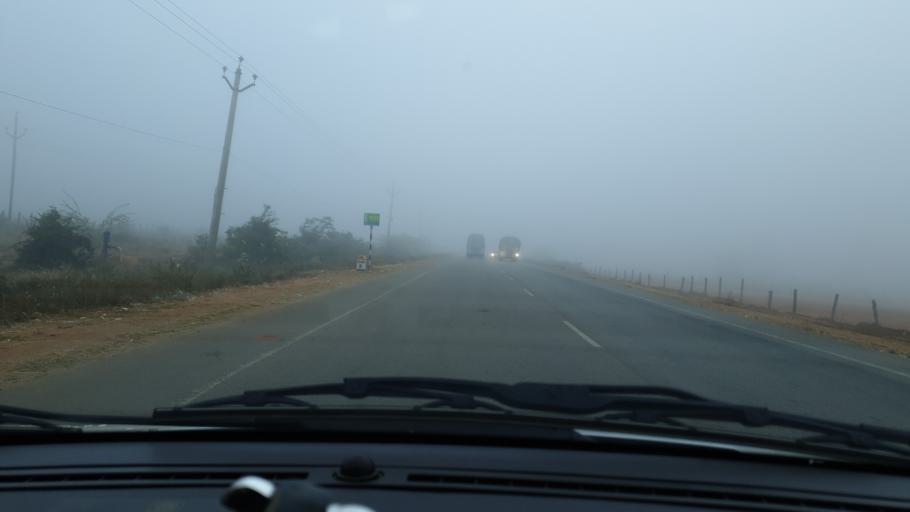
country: IN
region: Telangana
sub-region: Mahbubnagar
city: Nagar Karnul
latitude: 16.6630
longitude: 78.5387
